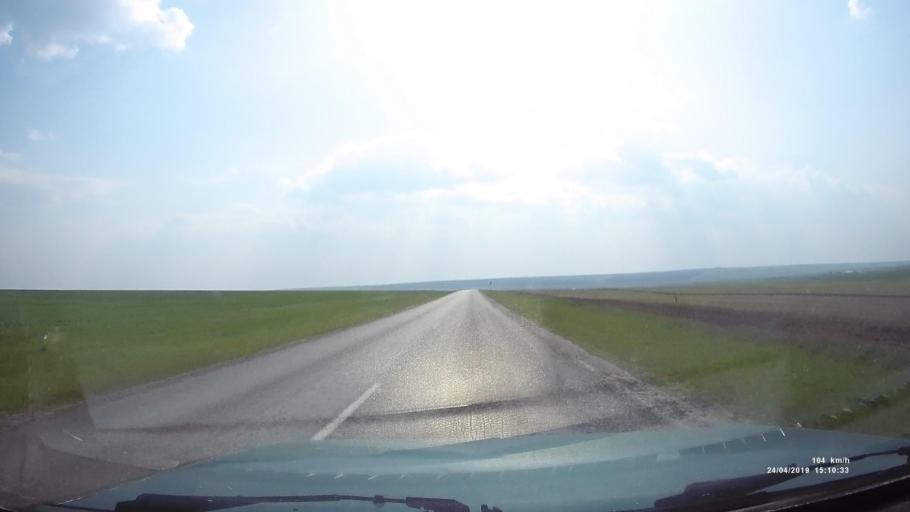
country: RU
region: Rostov
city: Remontnoye
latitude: 46.5488
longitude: 43.3390
